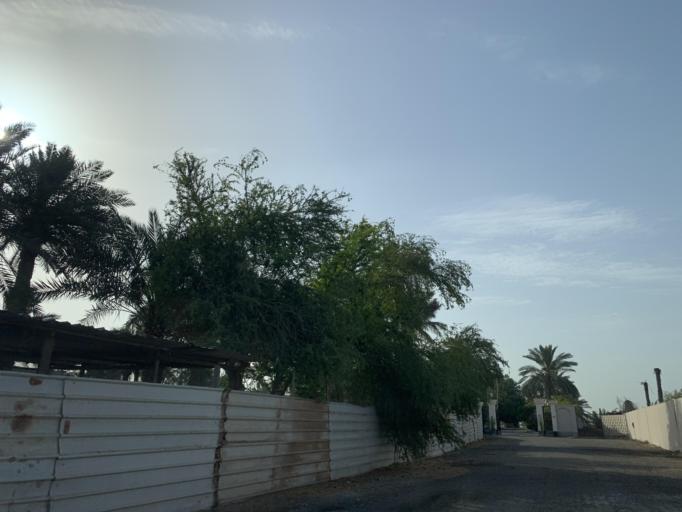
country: BH
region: Manama
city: Manama
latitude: 26.1804
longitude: 50.5855
